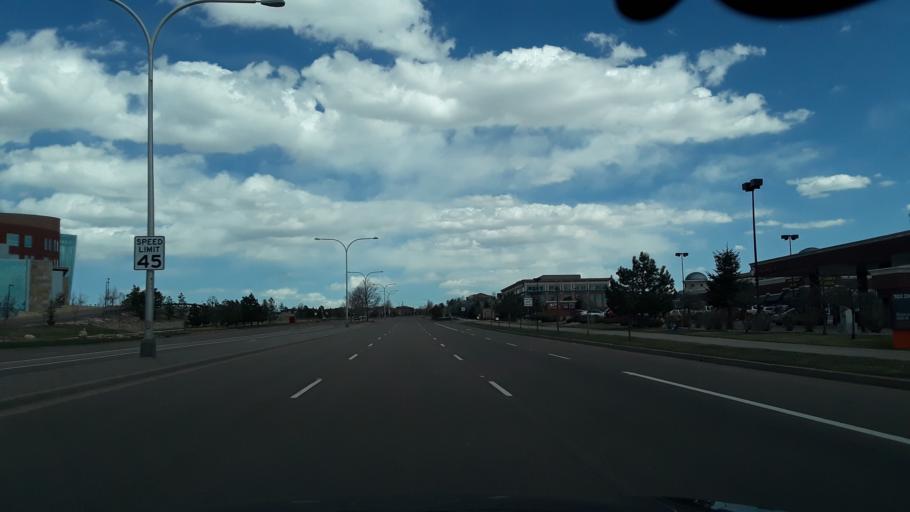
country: US
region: Colorado
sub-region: El Paso County
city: Black Forest
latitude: 38.9658
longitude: -104.7567
